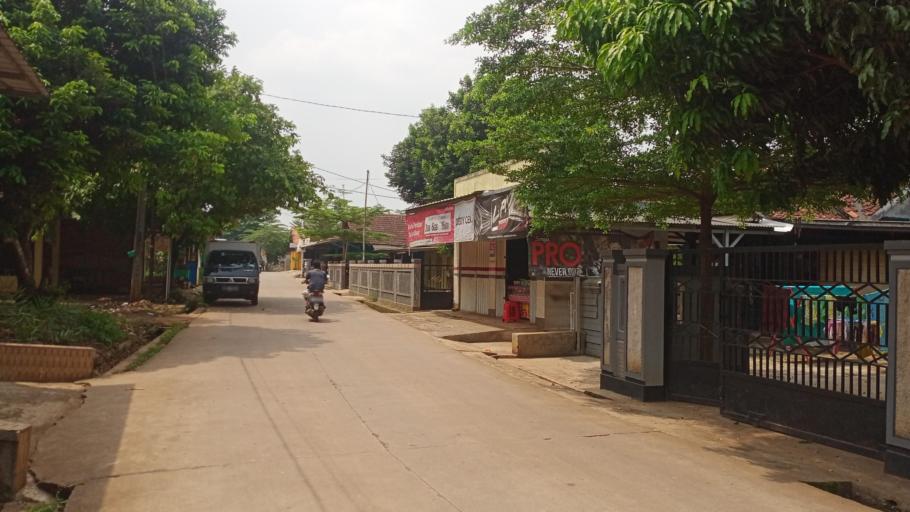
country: ID
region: West Java
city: Cileungsir
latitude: -6.3820
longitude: 107.0315
